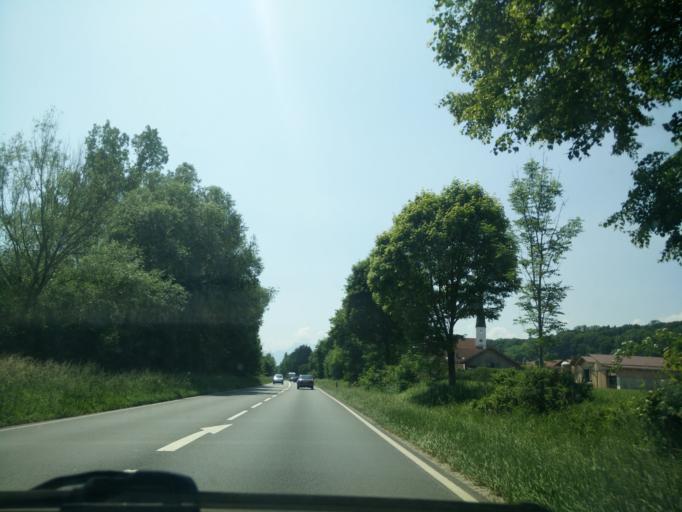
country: DE
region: Bavaria
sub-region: Upper Bavaria
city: Laufen
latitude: 47.9130
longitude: 12.9408
